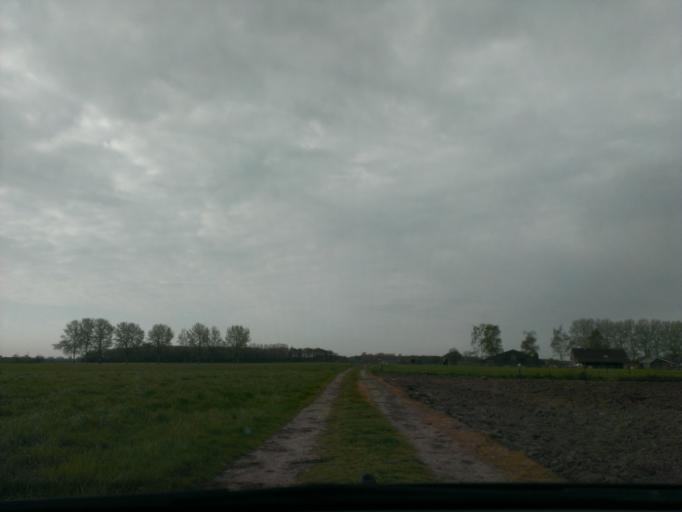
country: NL
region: Gelderland
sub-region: Gemeente Voorst
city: Twello
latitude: 52.2313
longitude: 6.0536
